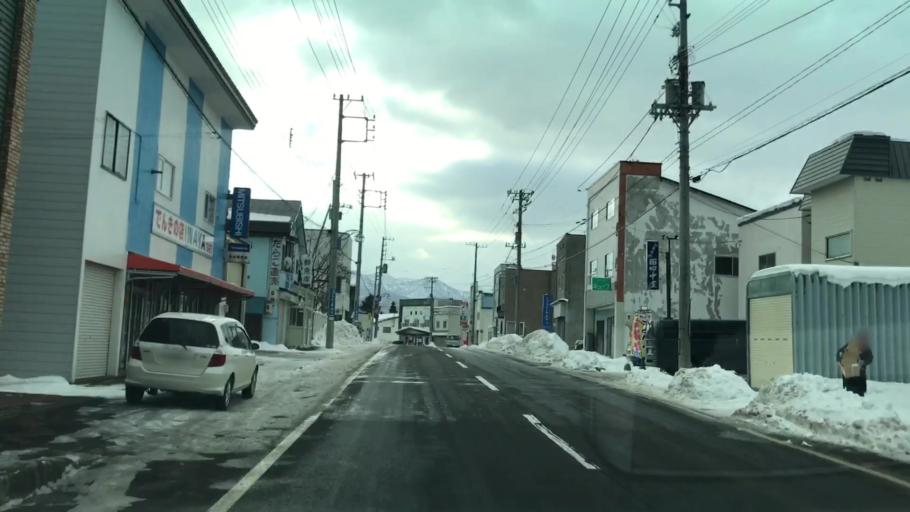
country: JP
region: Hokkaido
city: Yoichi
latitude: 43.2796
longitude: 140.6377
